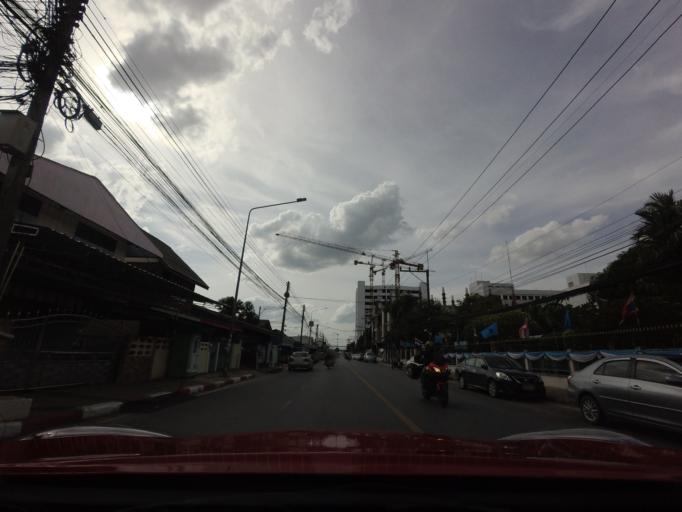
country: TH
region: Yala
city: Yala
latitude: 6.5459
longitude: 101.2770
